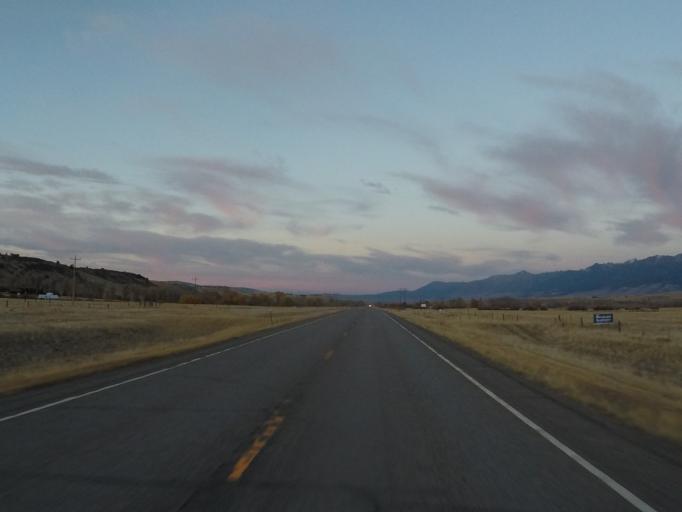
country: US
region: Montana
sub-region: Park County
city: Livingston
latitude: 45.3529
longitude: -110.7490
